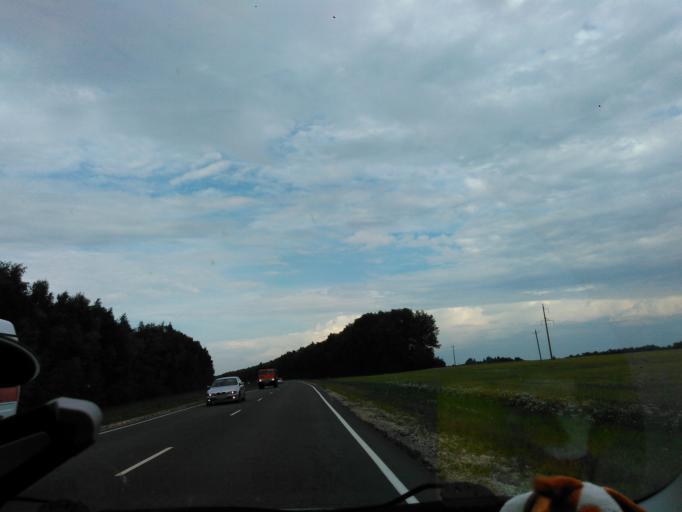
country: RU
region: Penza
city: Belinskiy
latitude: 52.9692
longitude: 43.5204
